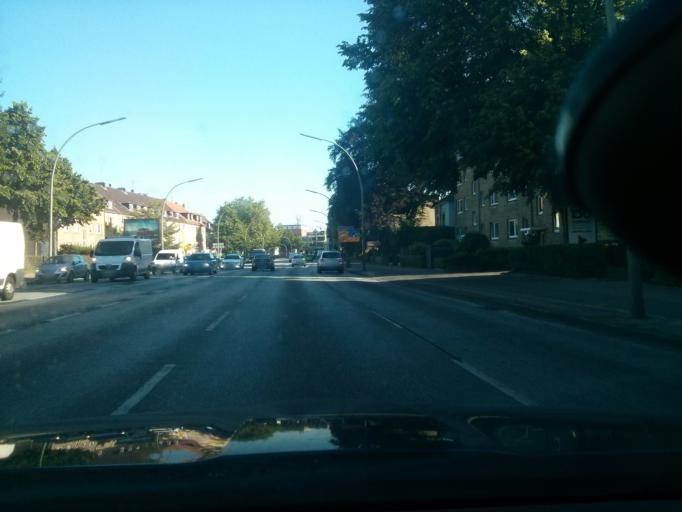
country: DE
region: Hamburg
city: Stellingen
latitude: 53.5891
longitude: 9.9312
